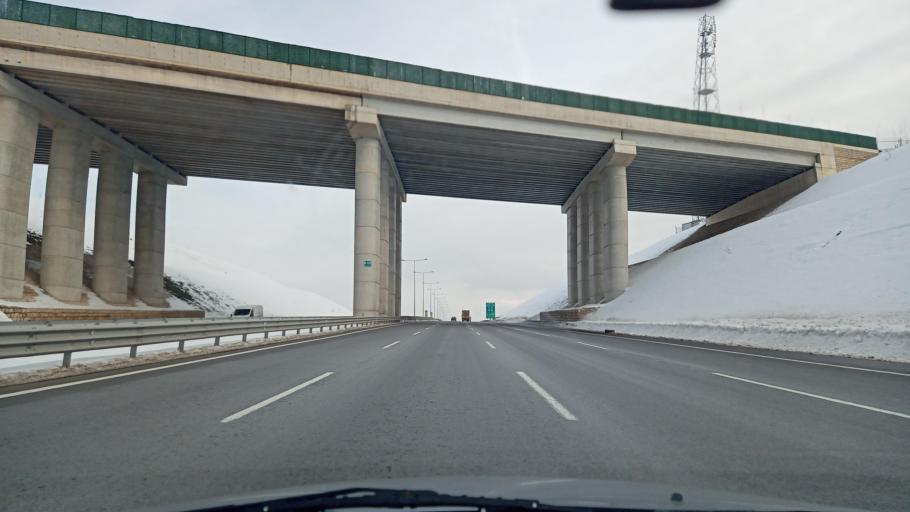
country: TR
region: Kocaeli
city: Hereke
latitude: 40.8908
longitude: 29.6899
